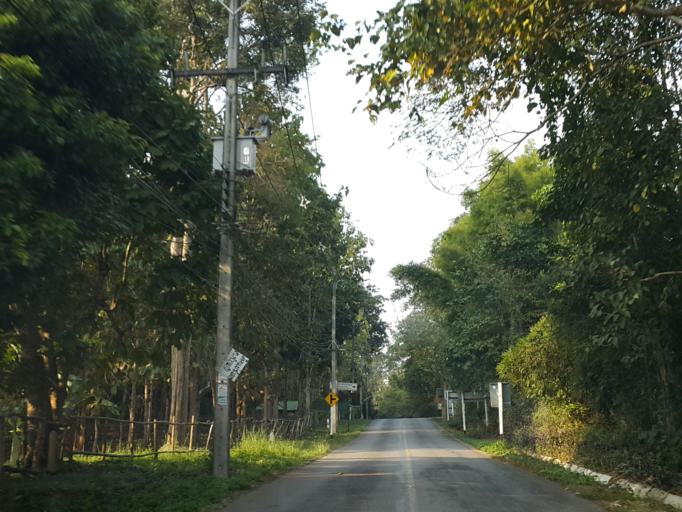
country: TH
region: Chiang Mai
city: Mae On
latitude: 18.8947
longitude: 99.2619
